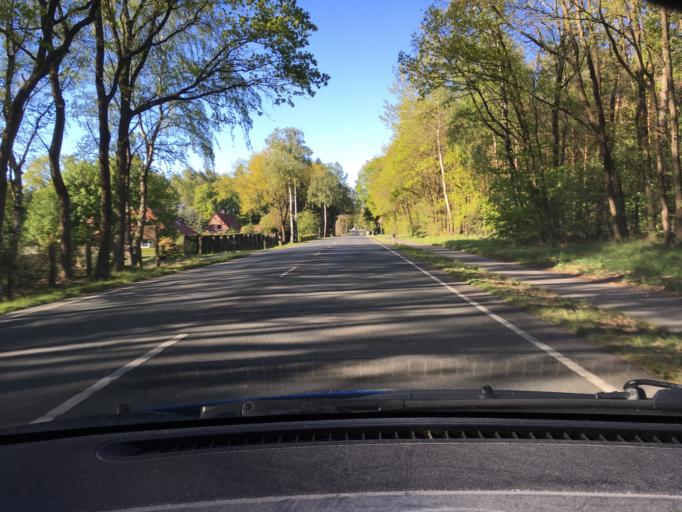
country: DE
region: Lower Saxony
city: Soltau
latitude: 53.0659
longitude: 9.8602
